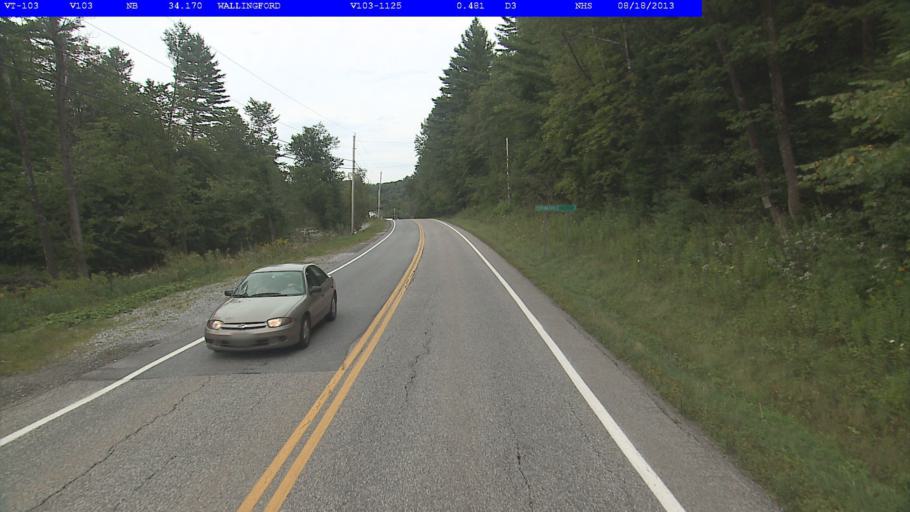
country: US
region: Vermont
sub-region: Rutland County
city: Rutland
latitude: 43.4537
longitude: -72.8784
